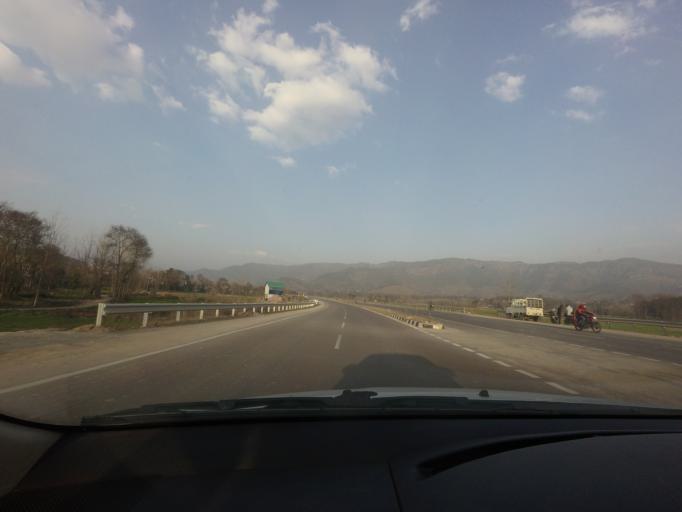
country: IN
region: Himachal Pradesh
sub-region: Mandi
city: Sundarnagar
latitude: 31.6126
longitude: 76.9348
